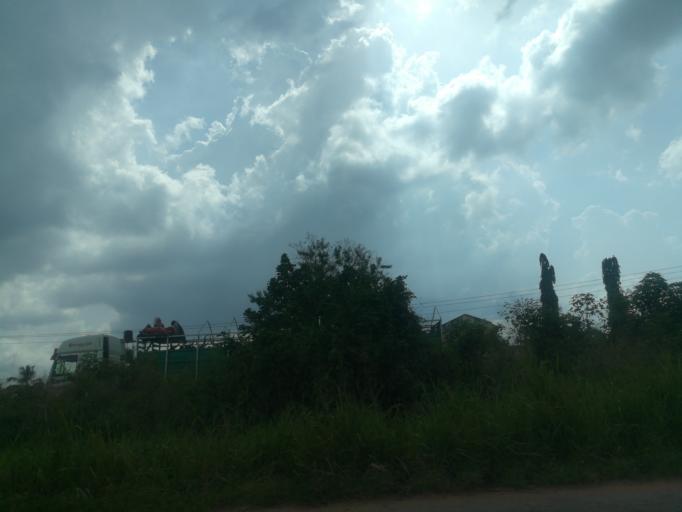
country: NG
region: Oyo
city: Ibadan
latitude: 7.4404
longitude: 3.9247
